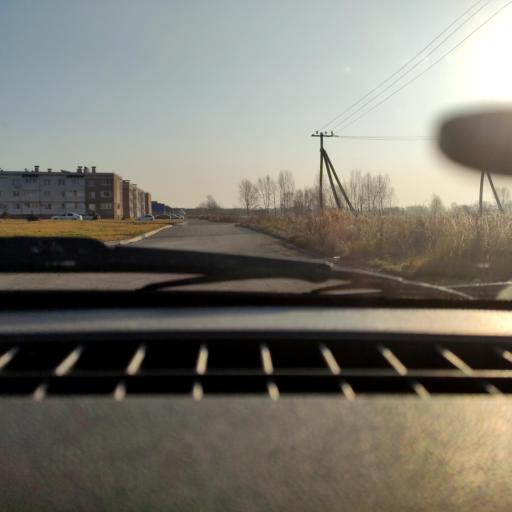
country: RU
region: Bashkortostan
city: Ufa
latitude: 54.8325
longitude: 56.1673
